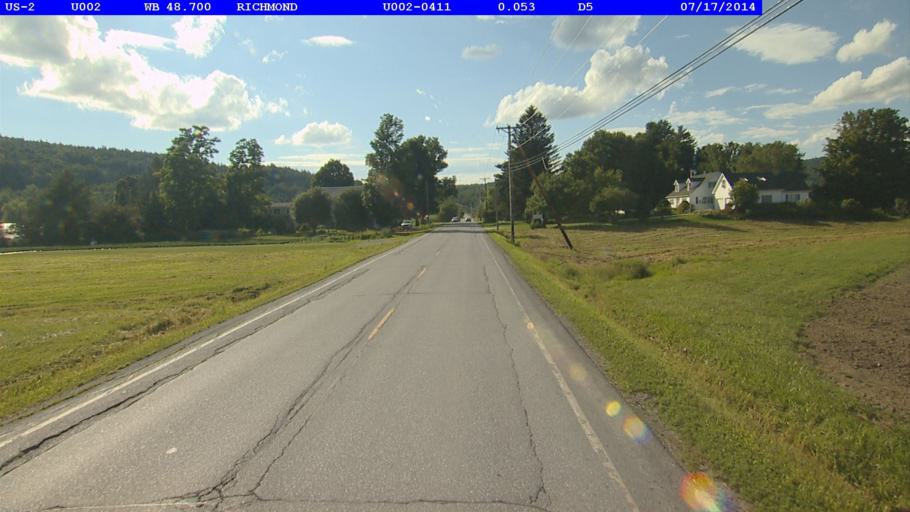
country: US
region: Vermont
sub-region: Chittenden County
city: Williston
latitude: 44.4286
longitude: -73.0275
